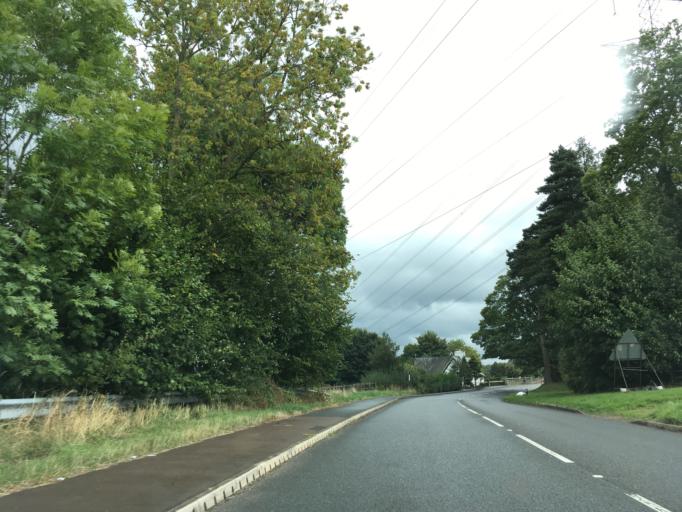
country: GB
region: Wales
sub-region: Monmouthshire
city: Gilwern
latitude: 51.8220
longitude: -3.0749
